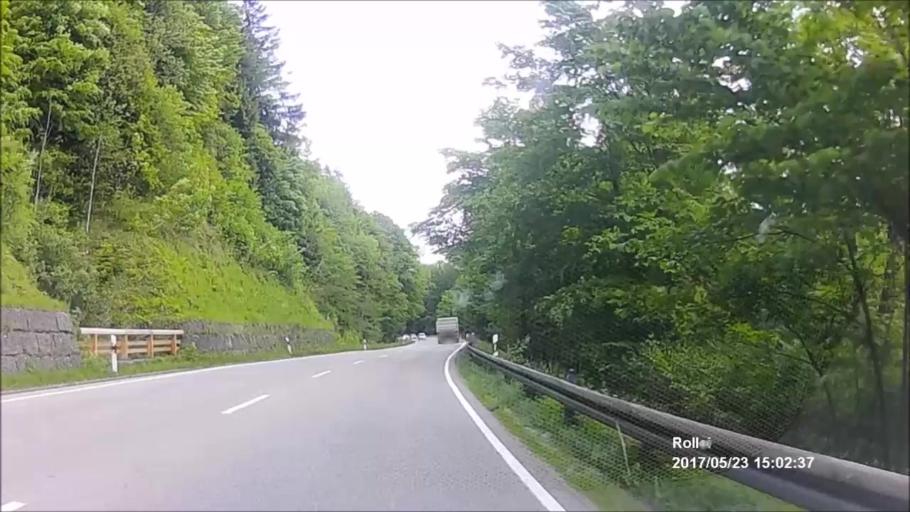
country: DE
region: Bavaria
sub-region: Upper Bavaria
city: Siegsdorf
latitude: 47.8429
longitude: 12.6402
